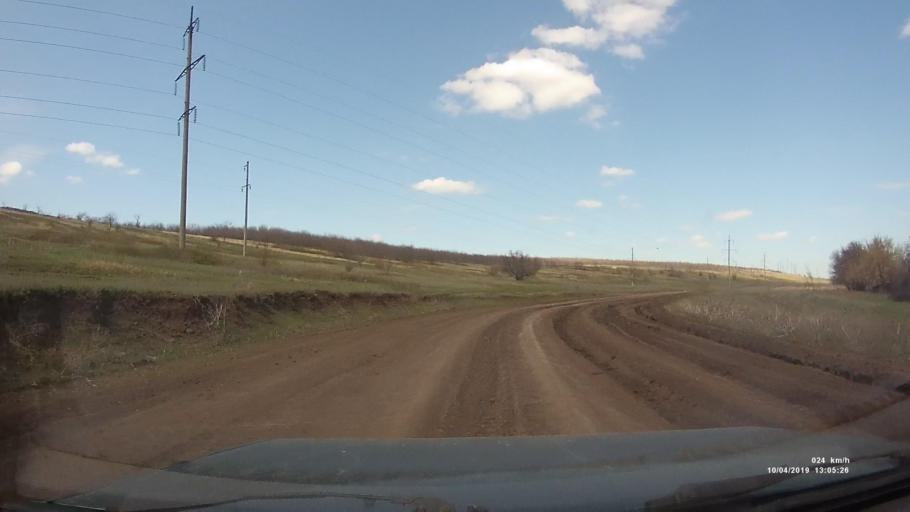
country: RU
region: Rostov
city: Masalovka
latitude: 48.3880
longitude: 40.2328
